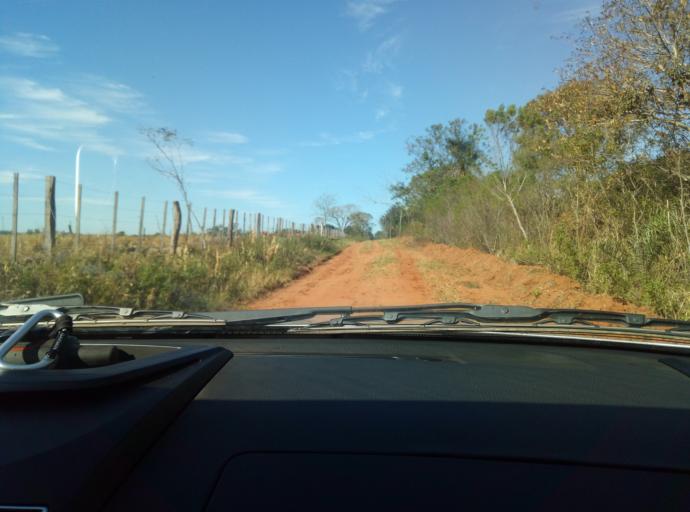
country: PY
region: Caaguazu
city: Carayao
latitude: -25.1693
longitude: -56.3054
